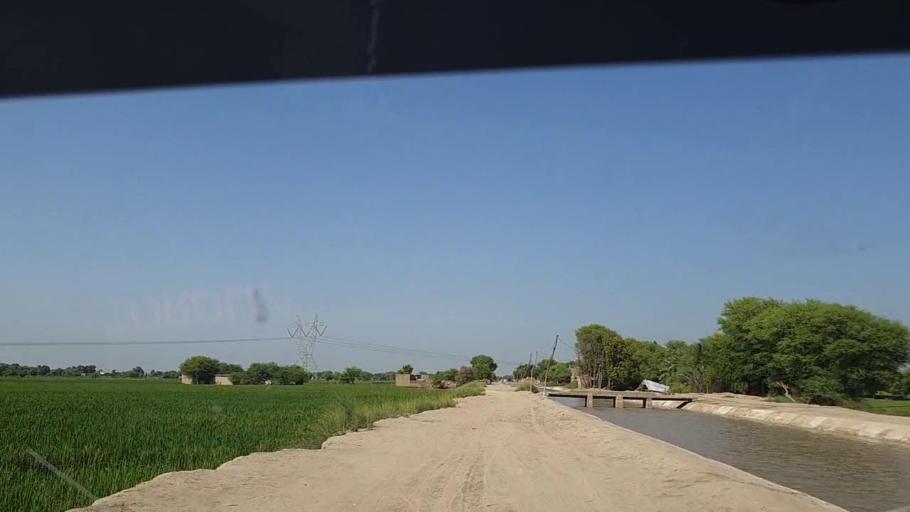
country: PK
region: Sindh
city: Ghauspur
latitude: 28.1664
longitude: 69.0963
